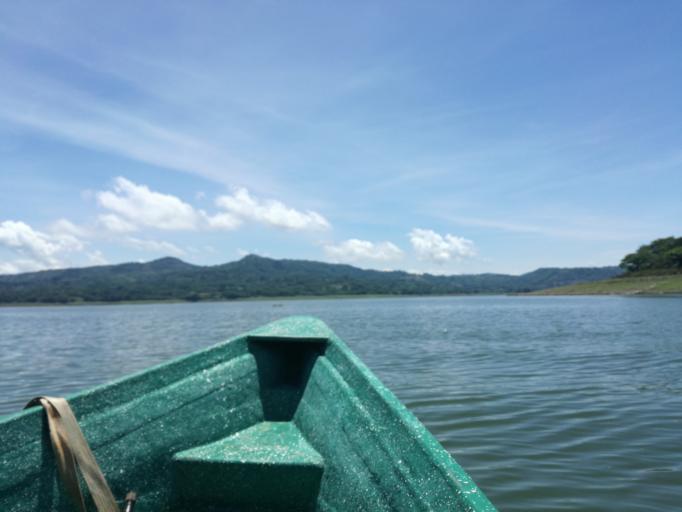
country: SV
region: Cuscatlan
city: Suchitoto
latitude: 13.9481
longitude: -89.0151
